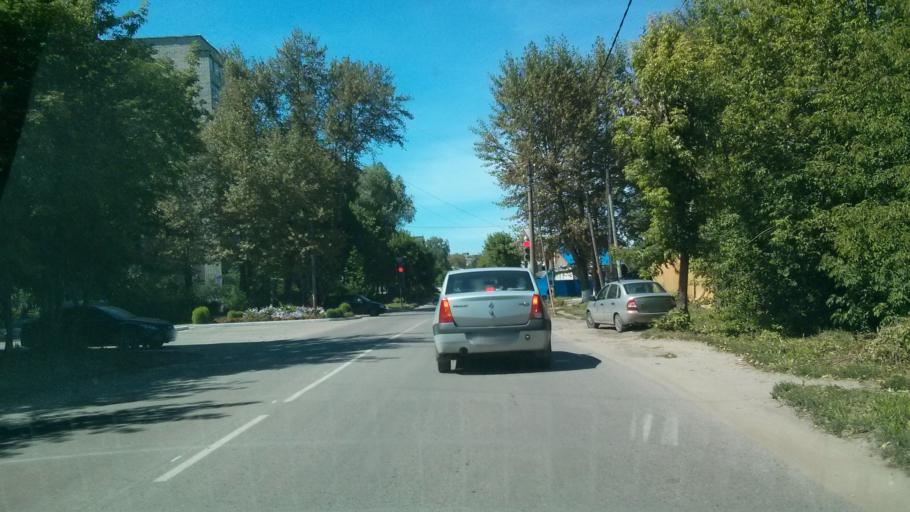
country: RU
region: Vladimir
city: Murom
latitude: 55.5682
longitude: 42.0248
